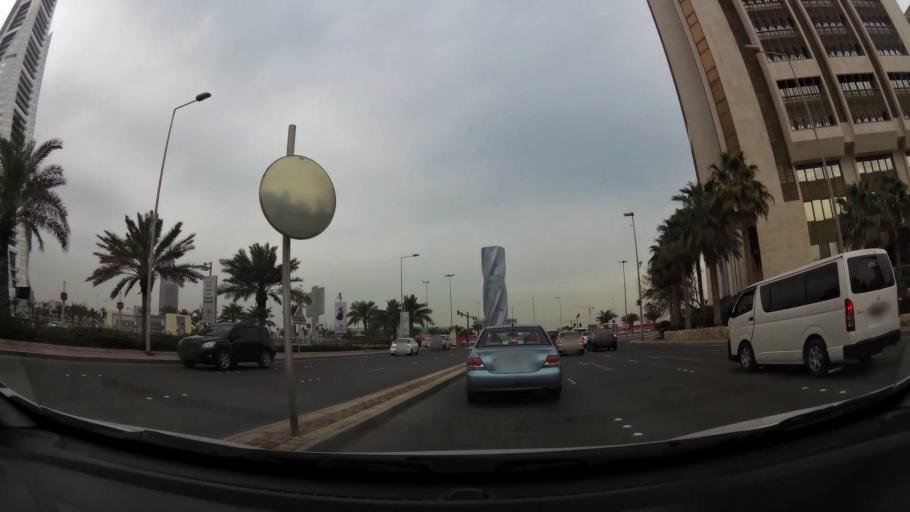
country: BH
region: Manama
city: Manama
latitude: 26.2405
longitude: 50.5835
